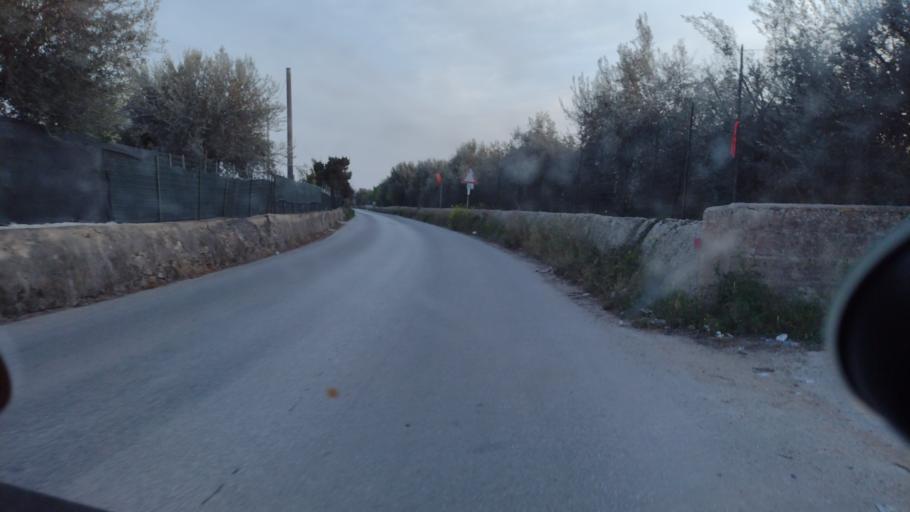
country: IT
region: Sicily
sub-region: Provincia di Siracusa
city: Avola
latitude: 36.8866
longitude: 15.1310
